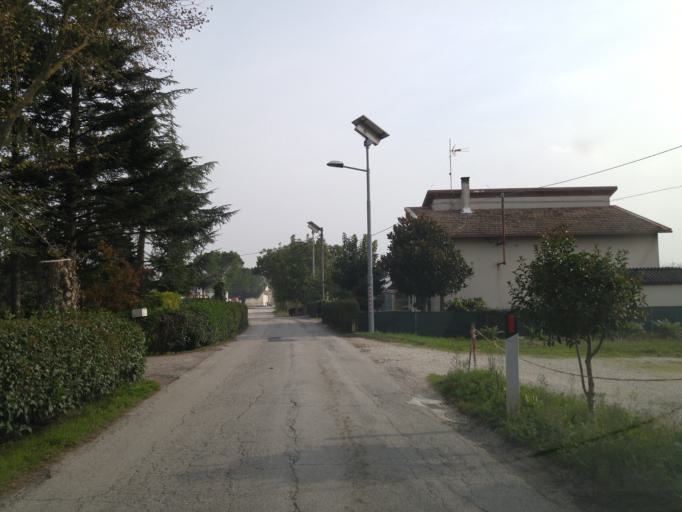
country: IT
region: The Marches
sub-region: Provincia di Pesaro e Urbino
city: Lucrezia
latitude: 43.7680
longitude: 12.9428
